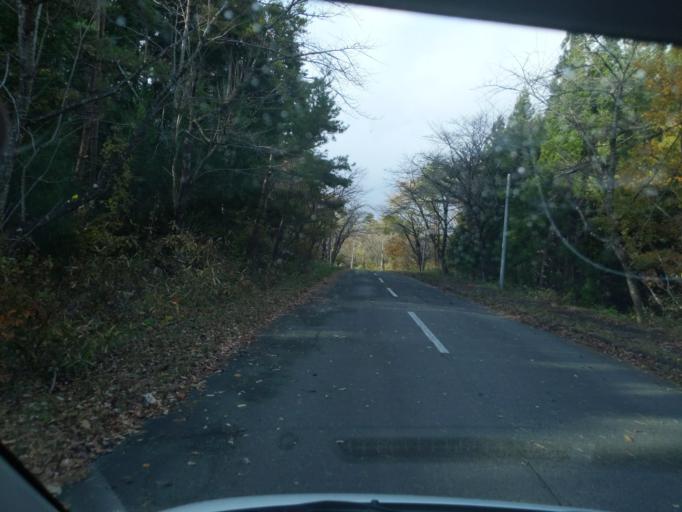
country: JP
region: Iwate
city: Mizusawa
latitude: 39.0316
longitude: 141.0873
